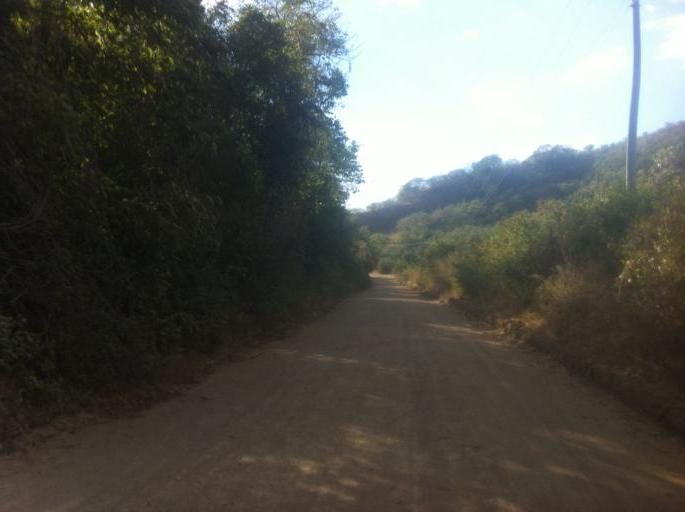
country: NI
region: Managua
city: Masachapa
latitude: 11.8101
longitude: -86.4933
